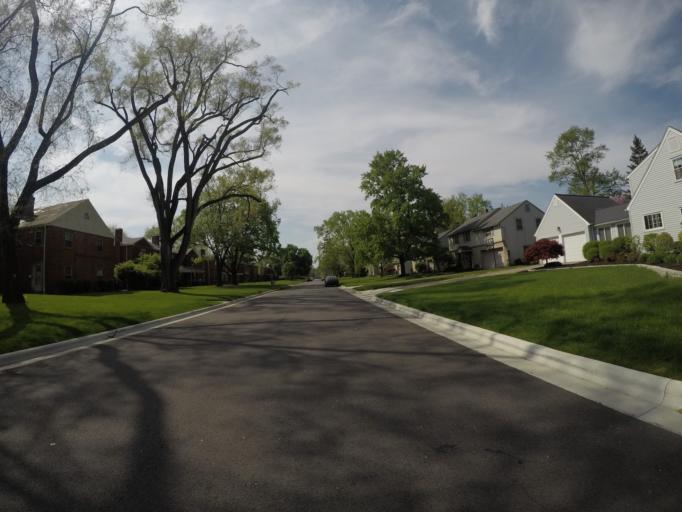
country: US
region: Ohio
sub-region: Franklin County
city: Upper Arlington
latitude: 39.9937
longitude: -83.0501
